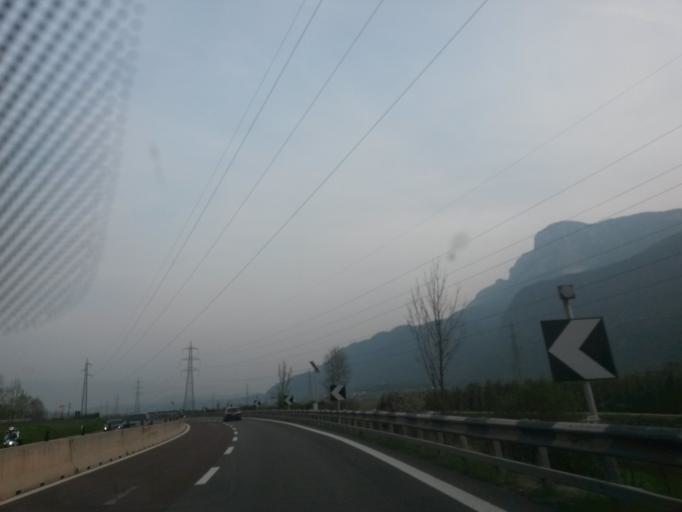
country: IT
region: Trentino-Alto Adige
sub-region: Bolzano
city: Nalles
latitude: 46.5450
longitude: 11.2238
